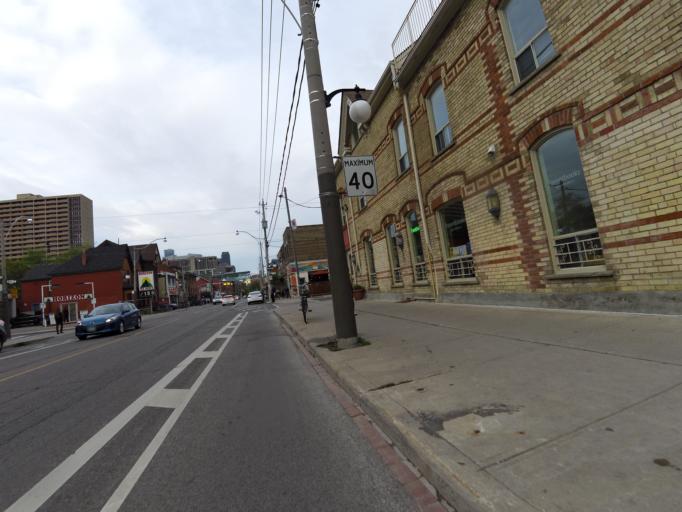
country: CA
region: Ontario
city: Toronto
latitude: 43.6624
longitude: -79.4052
